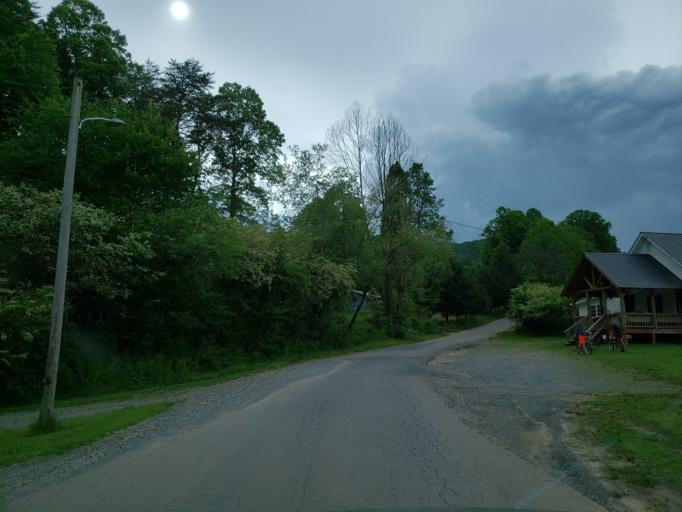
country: US
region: Georgia
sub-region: Fannin County
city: Blue Ridge
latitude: 34.8302
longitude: -84.4071
